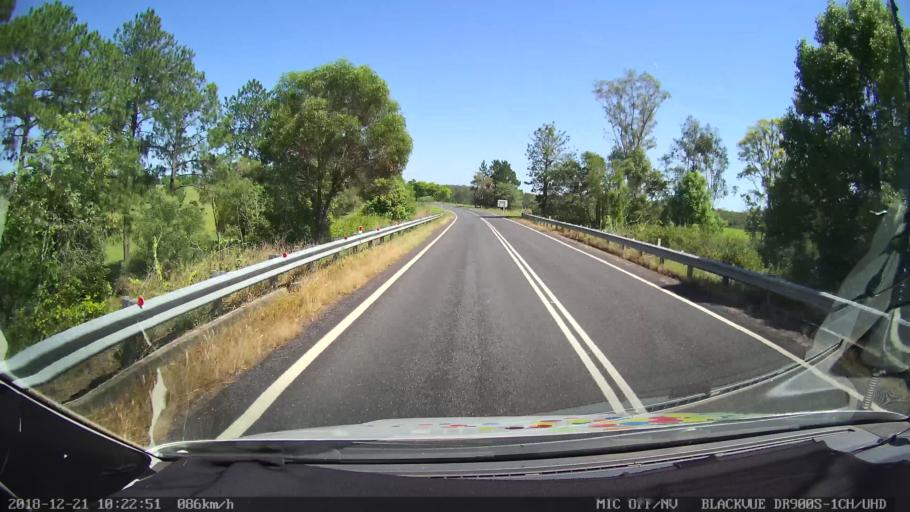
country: AU
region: New South Wales
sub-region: Clarence Valley
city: South Grafton
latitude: -29.6491
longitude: 152.7984
